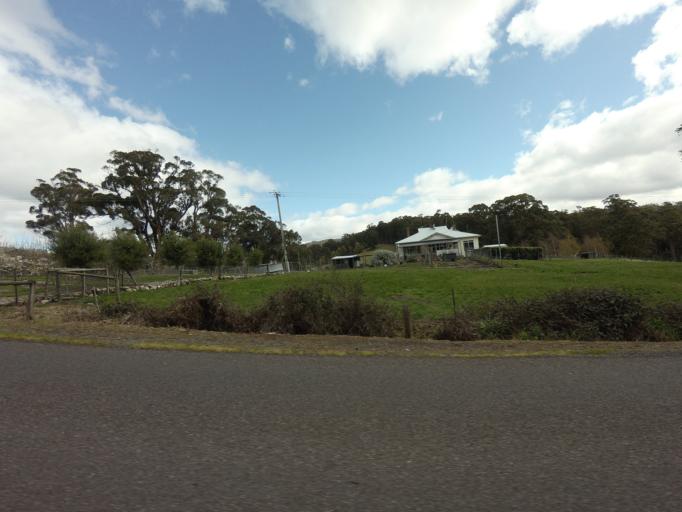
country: AU
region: Tasmania
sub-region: Huon Valley
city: Geeveston
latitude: -43.1952
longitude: 146.9420
